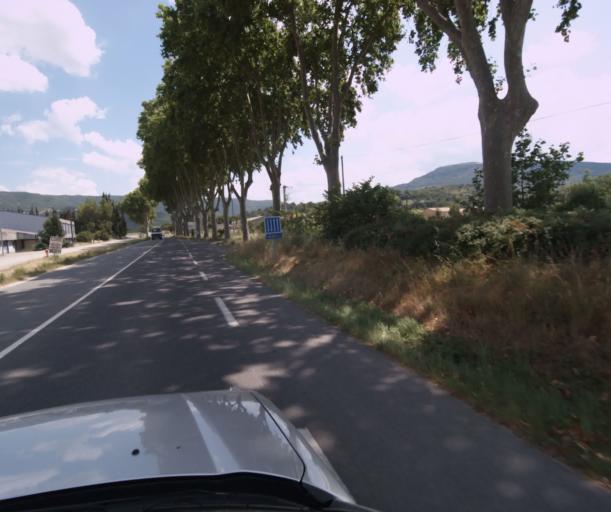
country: FR
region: Languedoc-Roussillon
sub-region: Departement de l'Aude
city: Limoux
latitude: 43.0423
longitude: 2.2398
